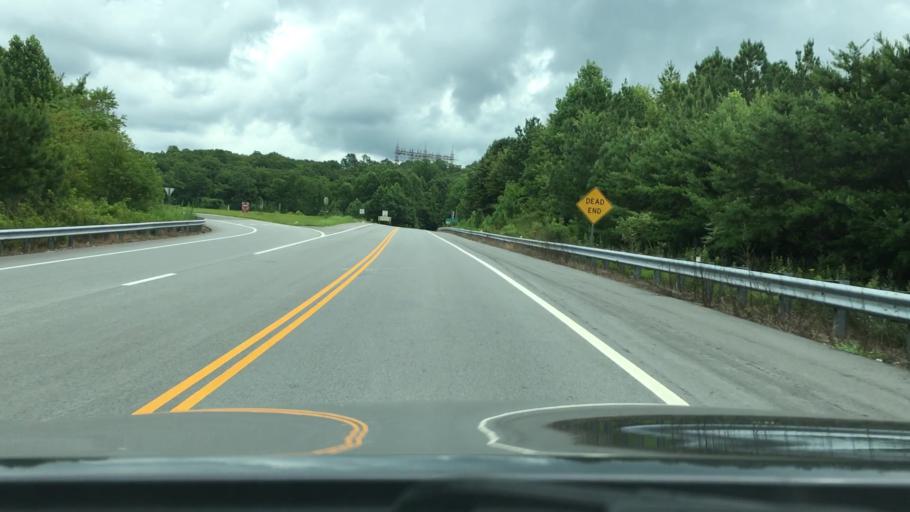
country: US
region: Virginia
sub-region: Amherst County
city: Madison Heights
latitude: 37.4071
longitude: -79.0823
